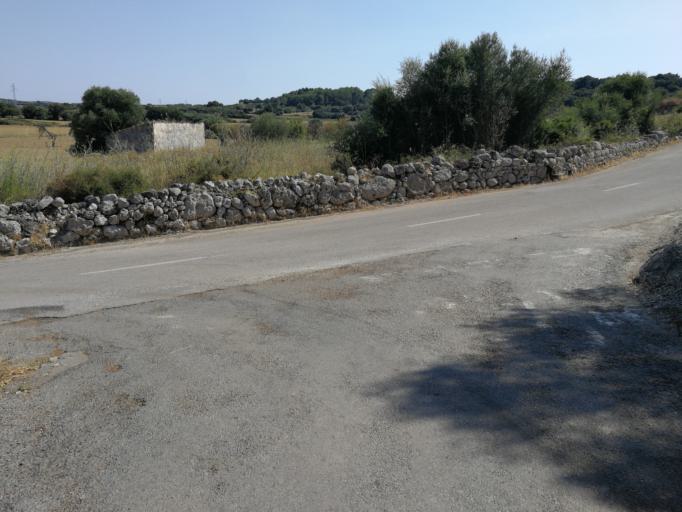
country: ES
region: Balearic Islands
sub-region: Illes Balears
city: Muro
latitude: 39.7344
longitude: 3.0737
